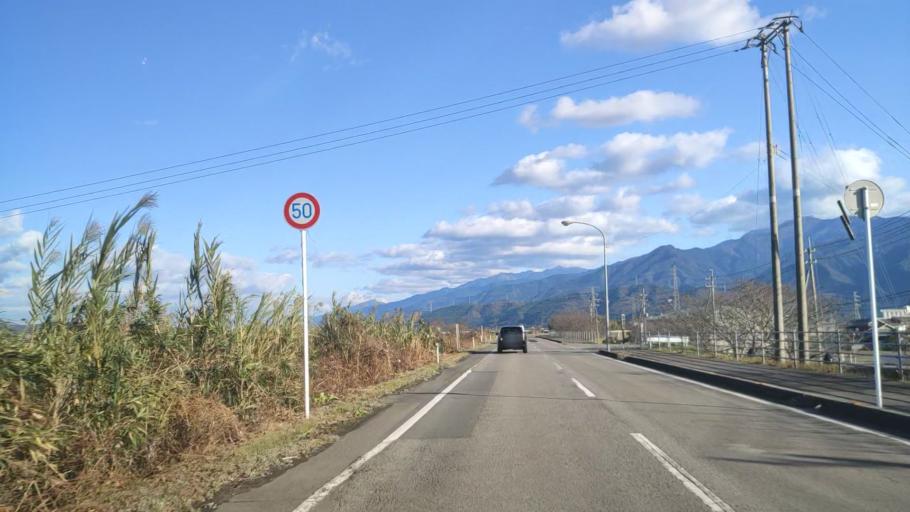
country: JP
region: Ehime
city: Saijo
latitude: 33.9109
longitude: 133.1636
